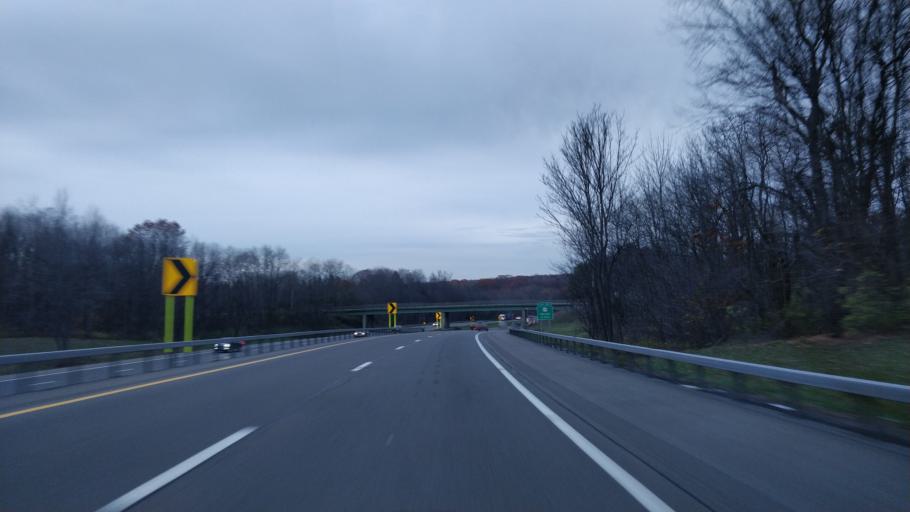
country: US
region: New York
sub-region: Oswego County
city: Central Square
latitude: 43.3717
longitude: -76.1219
